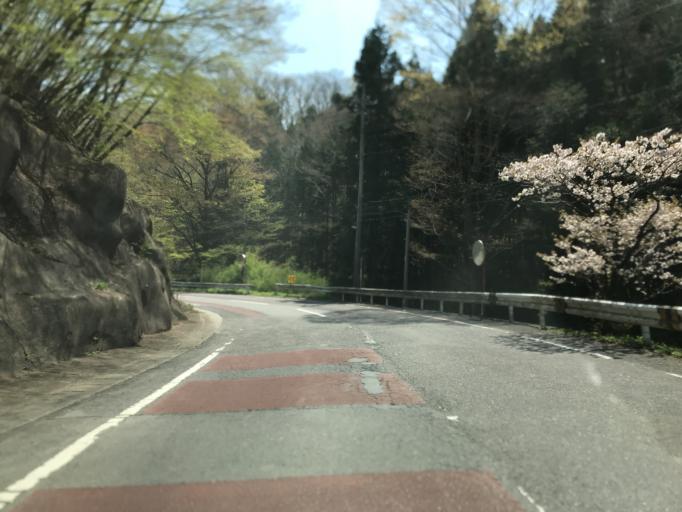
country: JP
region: Fukushima
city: Ishikawa
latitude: 37.0639
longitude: 140.4500
